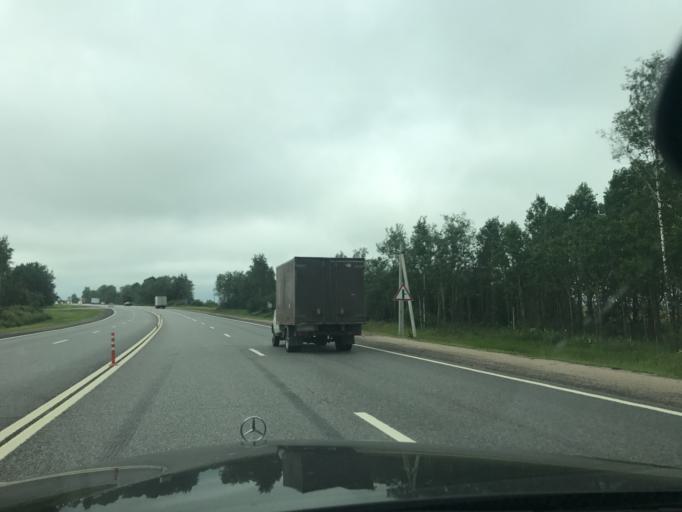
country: RU
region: Smolensk
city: Pechersk
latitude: 54.8605
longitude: 31.9009
